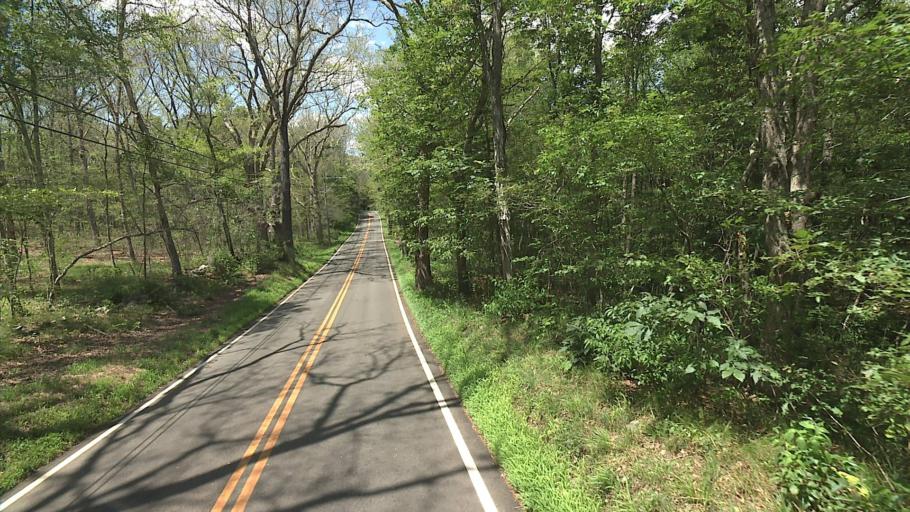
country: US
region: Connecticut
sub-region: Middlesex County
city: Essex Village
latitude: 41.4461
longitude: -72.3370
